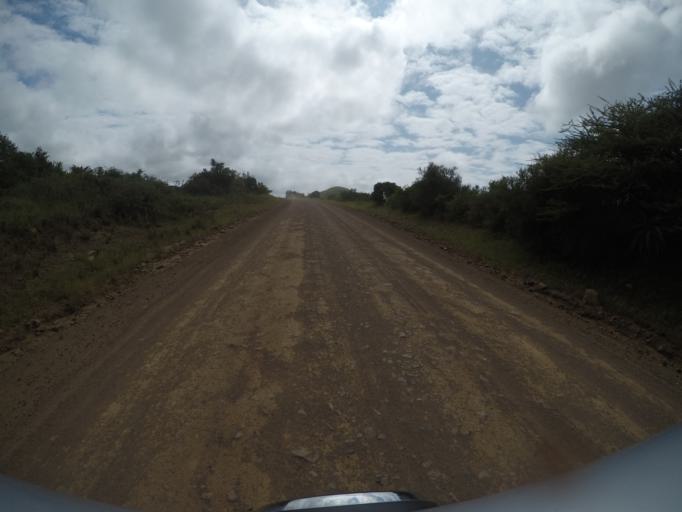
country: ZA
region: KwaZulu-Natal
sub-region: uThungulu District Municipality
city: Empangeni
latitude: -28.6100
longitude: 31.8460
